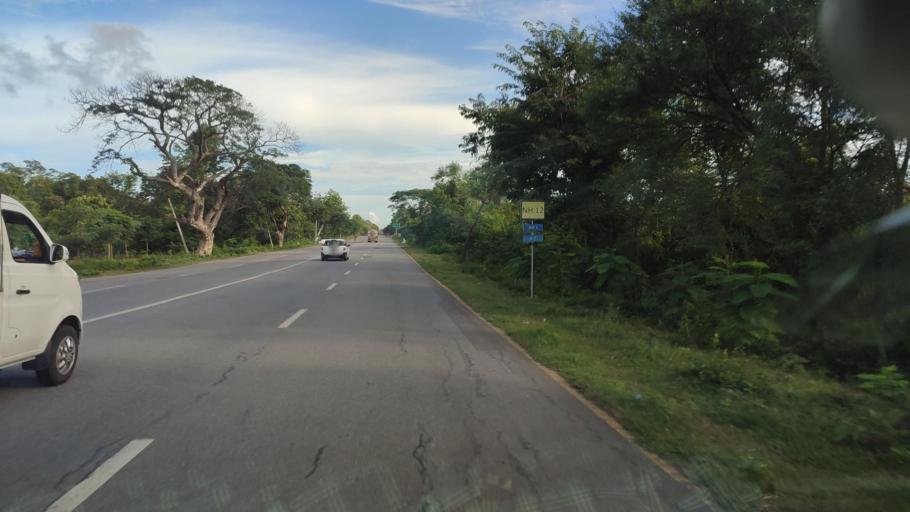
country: MM
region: Mandalay
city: Yamethin
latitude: 20.1624
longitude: 96.1903
